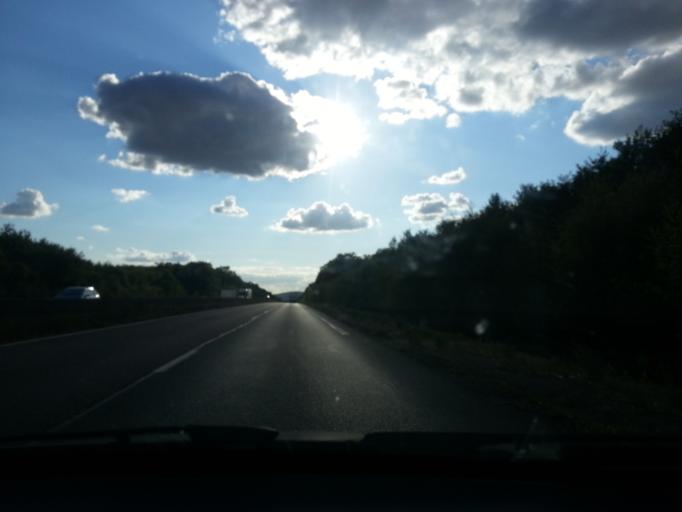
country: FR
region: Bourgogne
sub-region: Departement de Saone-et-Loire
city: Saint-Remy
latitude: 46.7559
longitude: 4.8045
